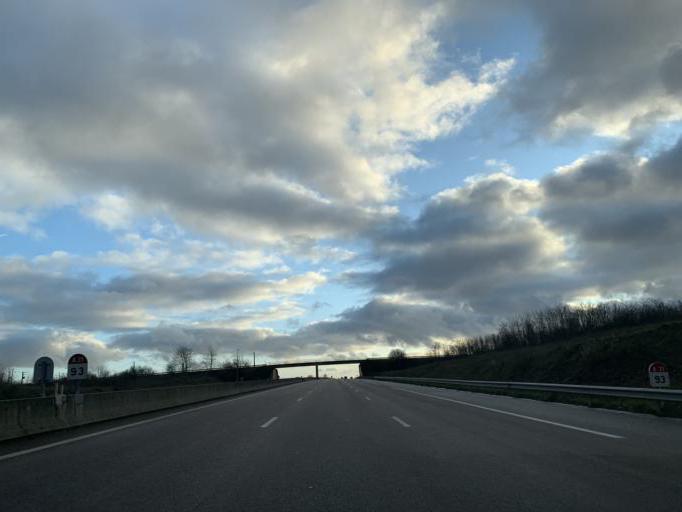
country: FR
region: Bourgogne
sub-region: Departement de la Cote-d'Or
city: Selongey
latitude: 47.7354
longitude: 5.1944
